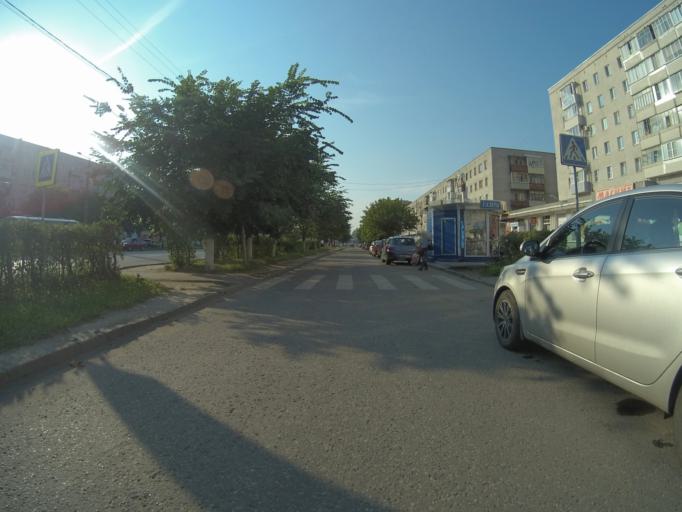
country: RU
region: Vladimir
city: Kommunar
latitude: 56.1701
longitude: 40.4623
